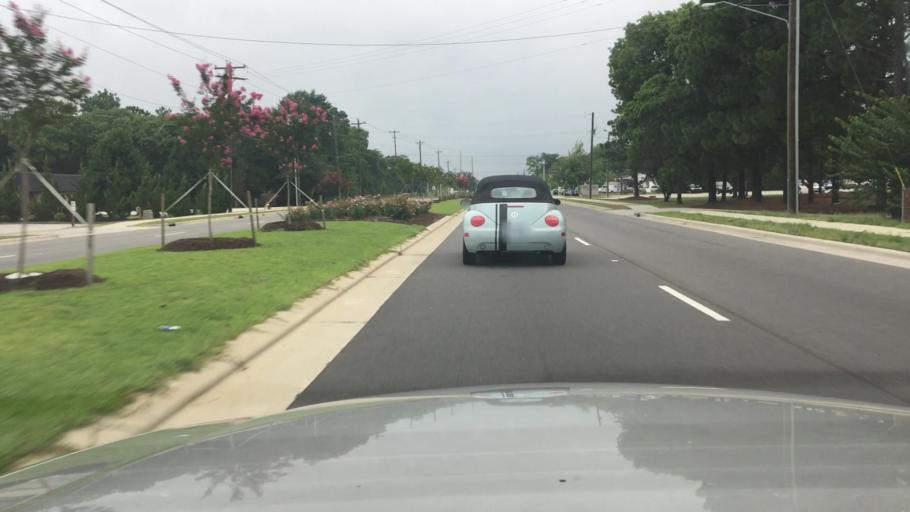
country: US
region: North Carolina
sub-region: Cumberland County
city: Fayetteville
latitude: 35.0125
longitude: -78.9088
